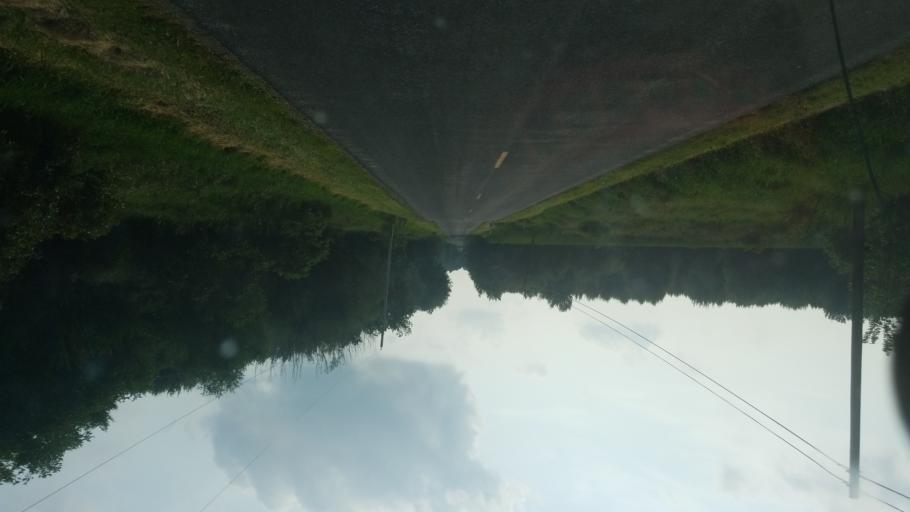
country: US
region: Ohio
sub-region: Medina County
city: Westfield Center
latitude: 41.0515
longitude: -81.9099
